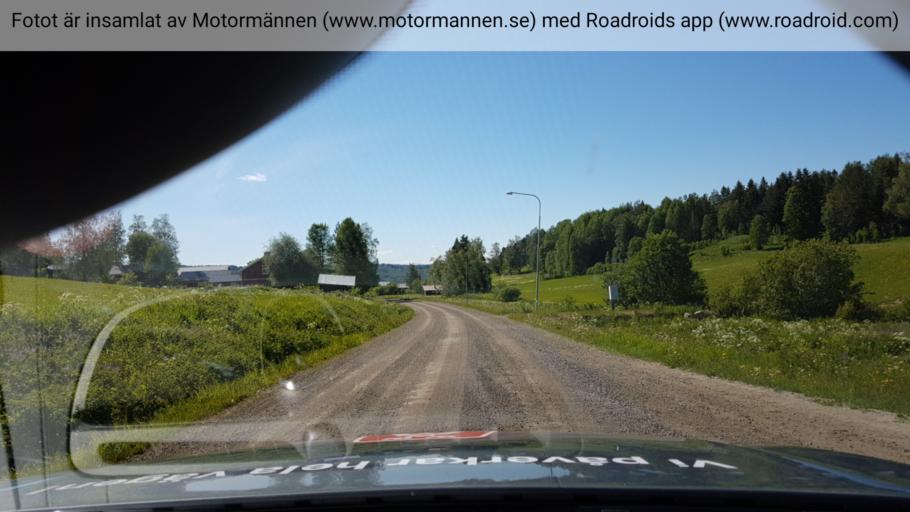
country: SE
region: Jaemtland
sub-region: OEstersunds Kommun
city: Brunflo
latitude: 62.9580
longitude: 14.9169
